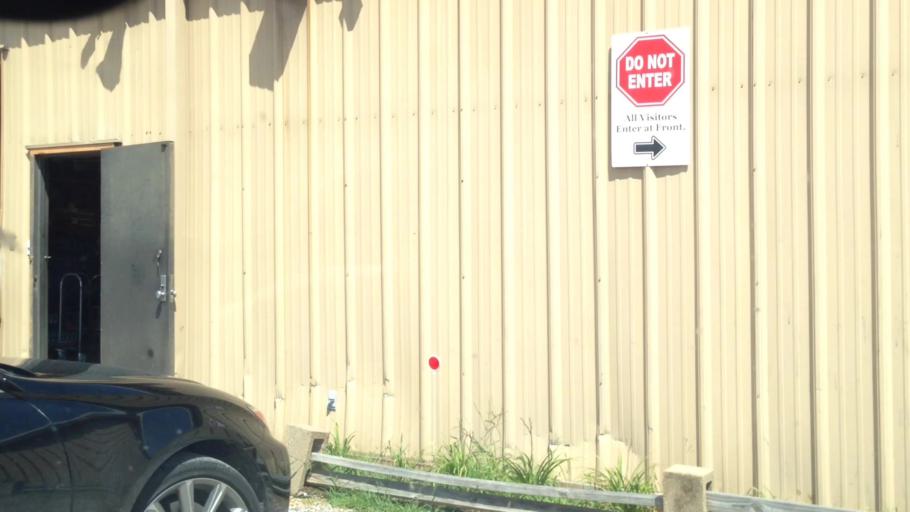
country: US
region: Louisiana
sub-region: Rapides Parish
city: Alexandria
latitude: 31.3133
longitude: -92.4808
